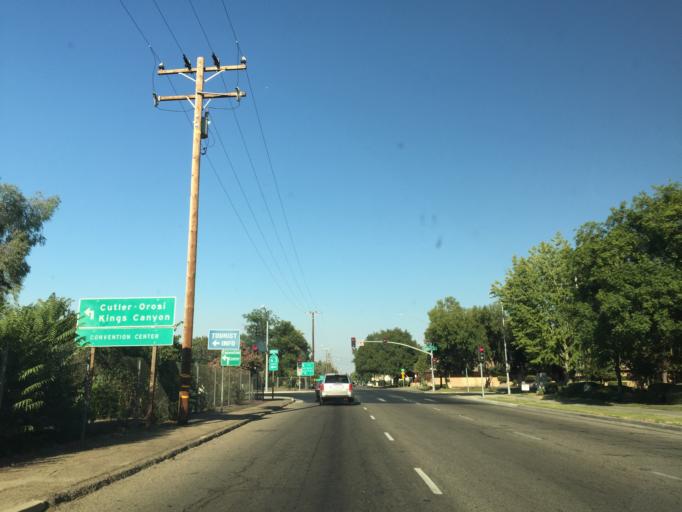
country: US
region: California
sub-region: Tulare County
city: Visalia
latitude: 36.3265
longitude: -119.2931
